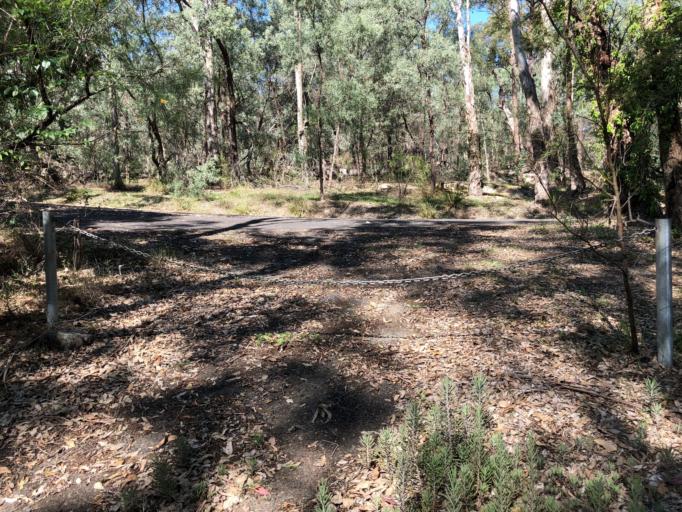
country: AU
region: New South Wales
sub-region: Hawkesbury
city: Scheyville
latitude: -33.5600
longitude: 150.9268
